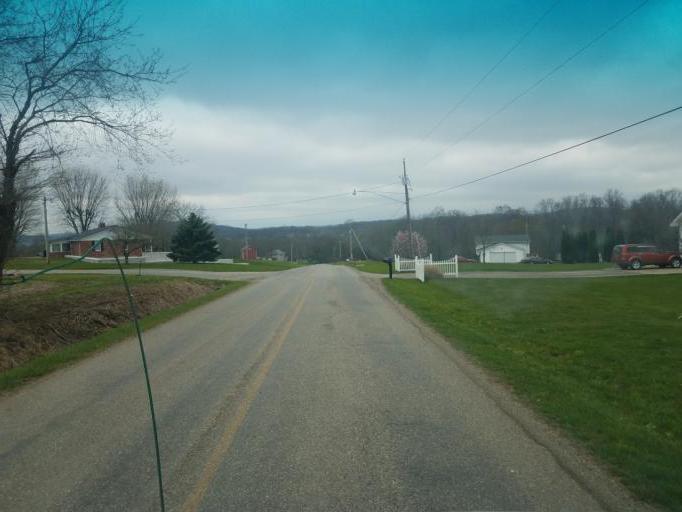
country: US
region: Ohio
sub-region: Stark County
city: Beach City
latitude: 40.5921
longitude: -81.6079
